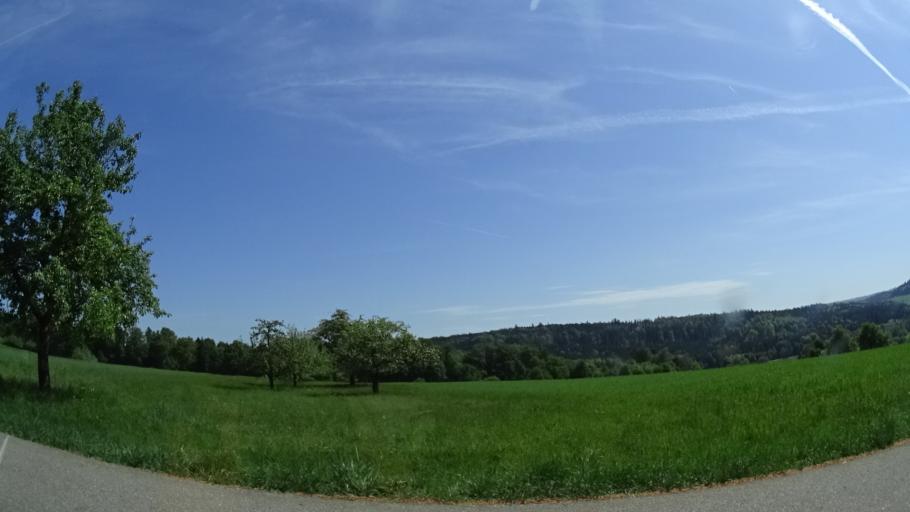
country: DE
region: Baden-Wuerttemberg
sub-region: Karlsruhe Region
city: Gaggenau
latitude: 48.8407
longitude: 8.3805
